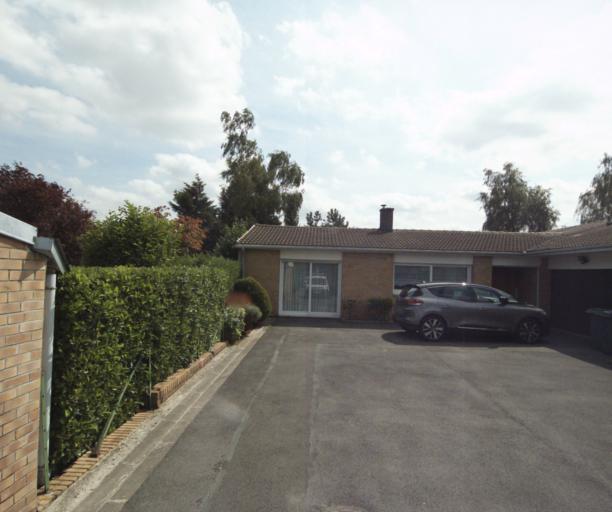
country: FR
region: Nord-Pas-de-Calais
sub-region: Departement du Nord
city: Hem
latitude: 50.6567
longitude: 3.2001
